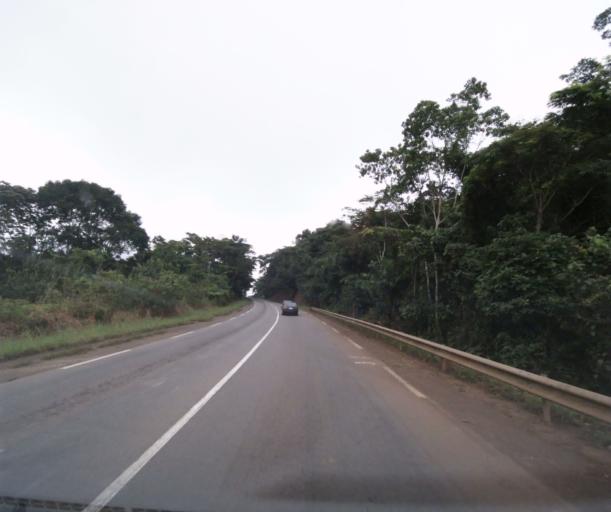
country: CM
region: Centre
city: Mbankomo
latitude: 3.7845
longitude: 11.2578
